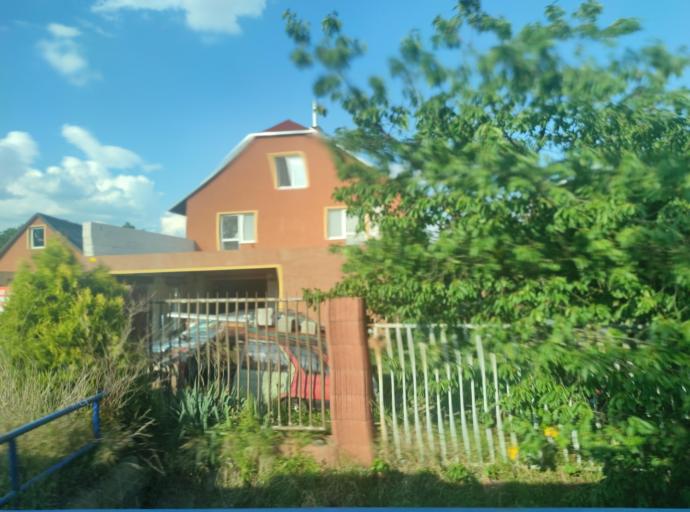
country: CZ
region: South Moravian
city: Vinicne Sumice
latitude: 49.1843
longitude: 16.8432
